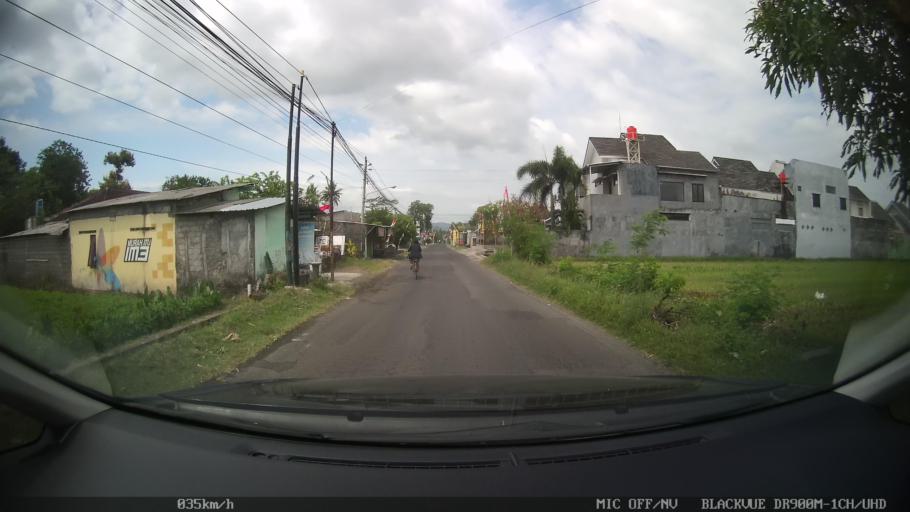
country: ID
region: Daerah Istimewa Yogyakarta
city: Depok
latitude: -7.7831
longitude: 110.4640
